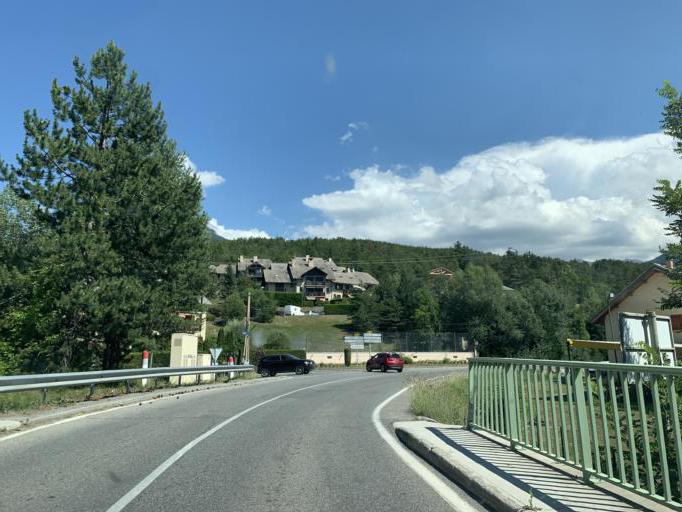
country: FR
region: Provence-Alpes-Cote d'Azur
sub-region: Departement des Hautes-Alpes
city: Embrun
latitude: 44.5419
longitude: 6.4971
